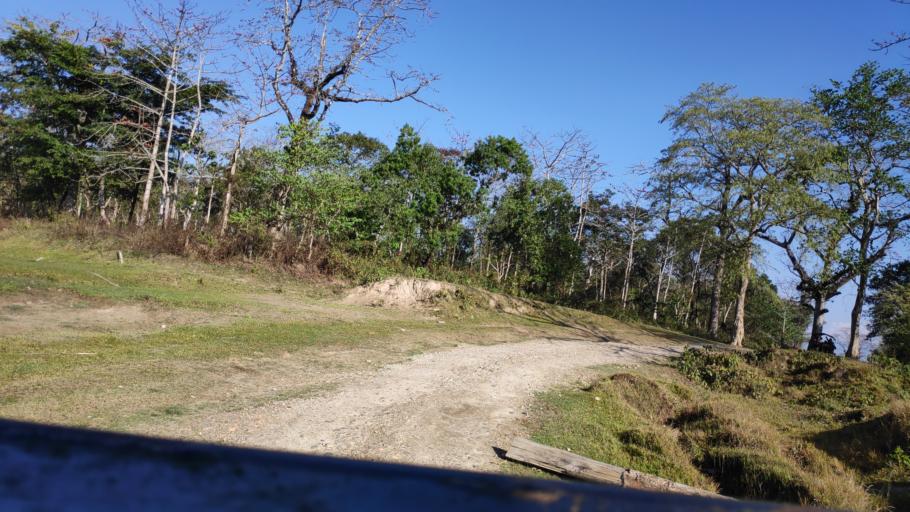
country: NP
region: Central Region
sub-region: Narayani Zone
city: Bharatpur
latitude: 27.5627
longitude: 84.5218
